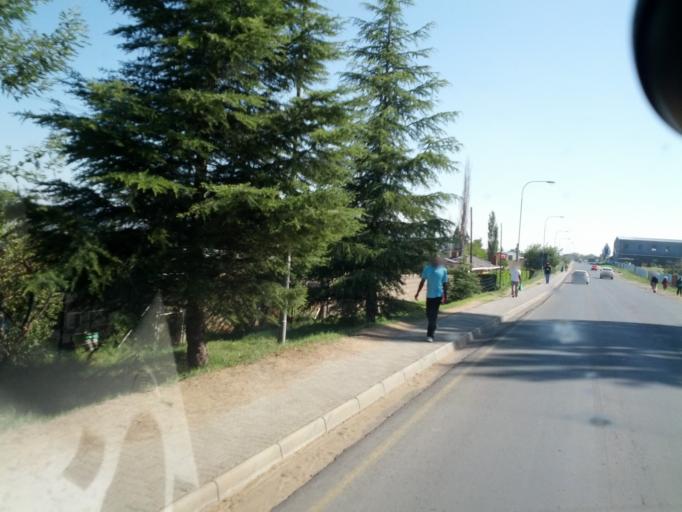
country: LS
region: Maseru
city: Maseru
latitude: -29.3069
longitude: 27.4987
